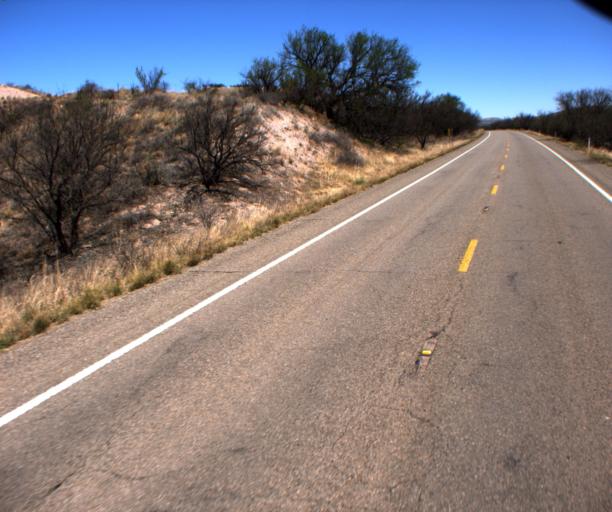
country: US
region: Arizona
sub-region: Santa Cruz County
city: Rio Rico
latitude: 31.5560
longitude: -110.7357
